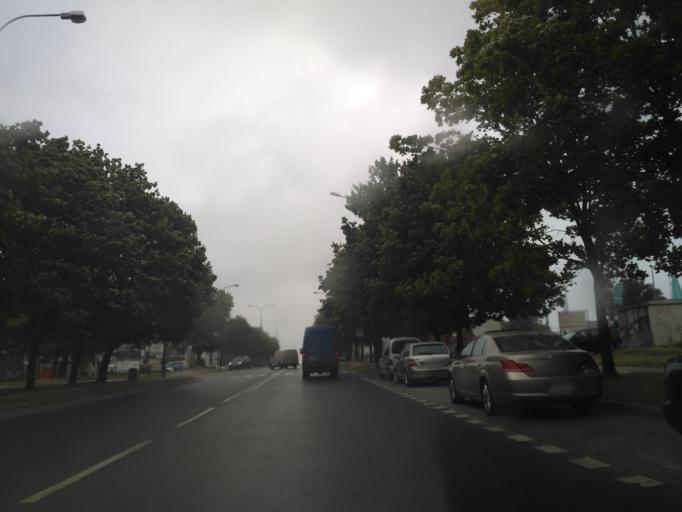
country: PL
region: Lublin Voivodeship
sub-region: Powiat lubelski
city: Lublin
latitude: 51.2699
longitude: 22.5652
